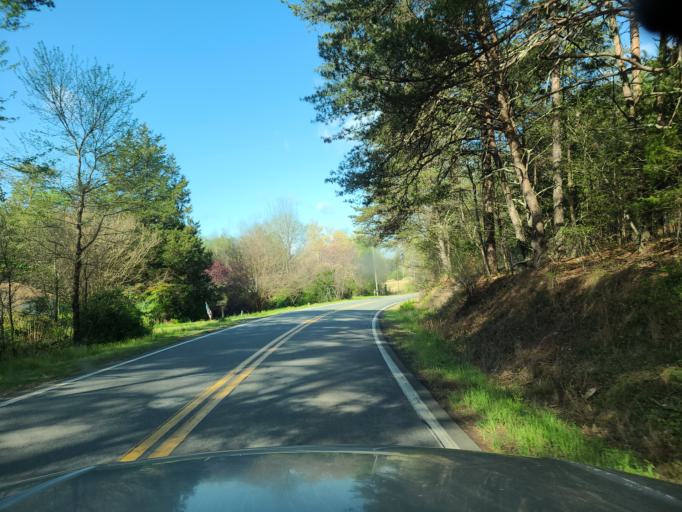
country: US
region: North Carolina
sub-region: Rutherford County
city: Forest City
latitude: 35.4087
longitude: -81.8625
